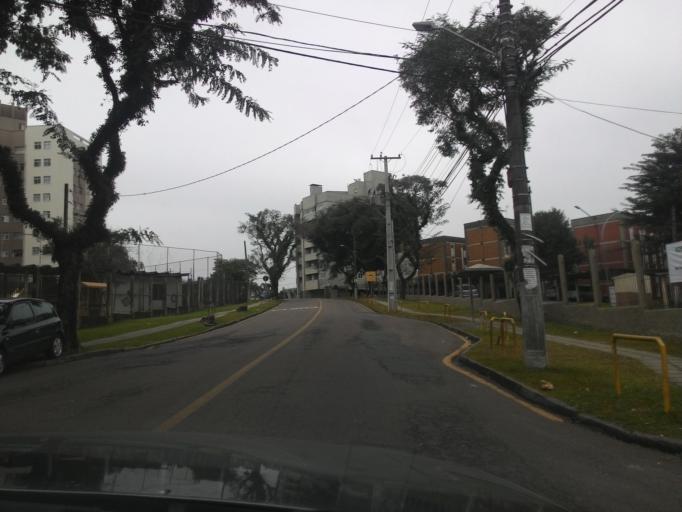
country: BR
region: Parana
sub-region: Curitiba
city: Curitiba
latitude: -25.4827
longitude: -49.2883
